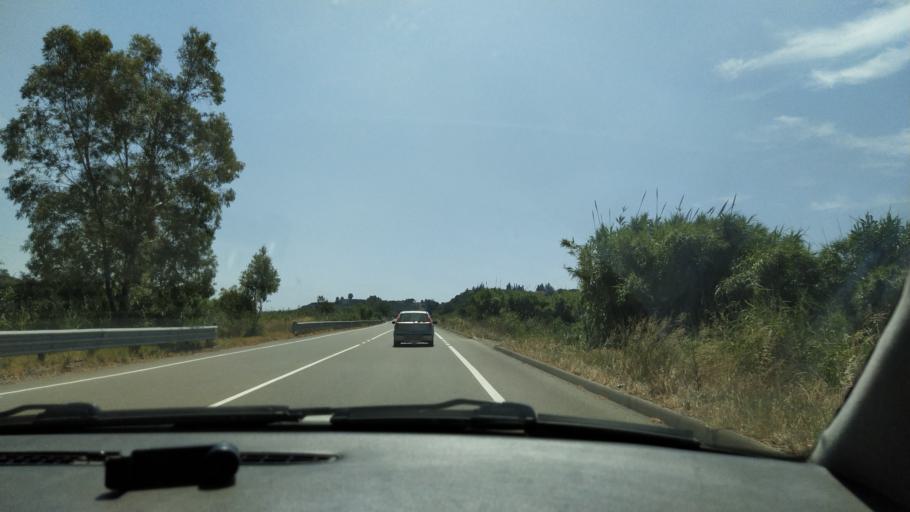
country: IT
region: Apulia
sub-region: Provincia di Taranto
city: Marina di Ginosa
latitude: 40.4359
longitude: 16.7881
